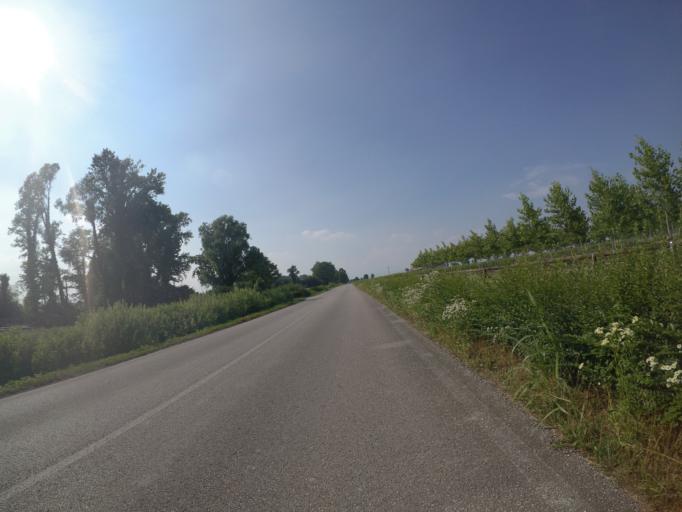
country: IT
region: Friuli Venezia Giulia
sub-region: Provincia di Udine
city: Camino al Tagliamento
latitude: 45.9247
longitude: 12.9635
